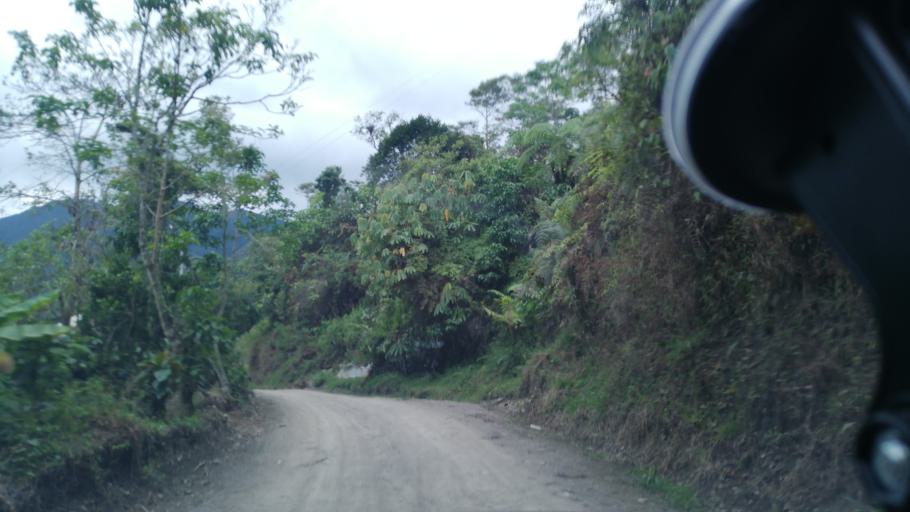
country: CO
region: Cundinamarca
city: Pacho
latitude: 5.1576
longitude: -74.2510
